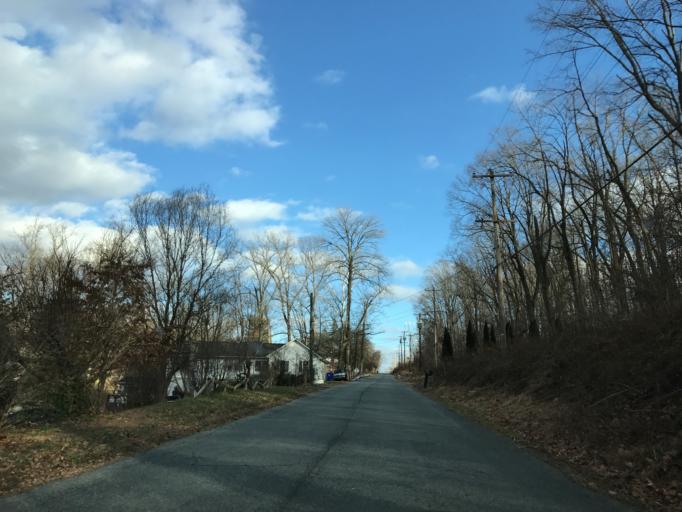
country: US
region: Maryland
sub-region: Cecil County
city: Rising Sun
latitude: 39.6938
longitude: -76.1228
